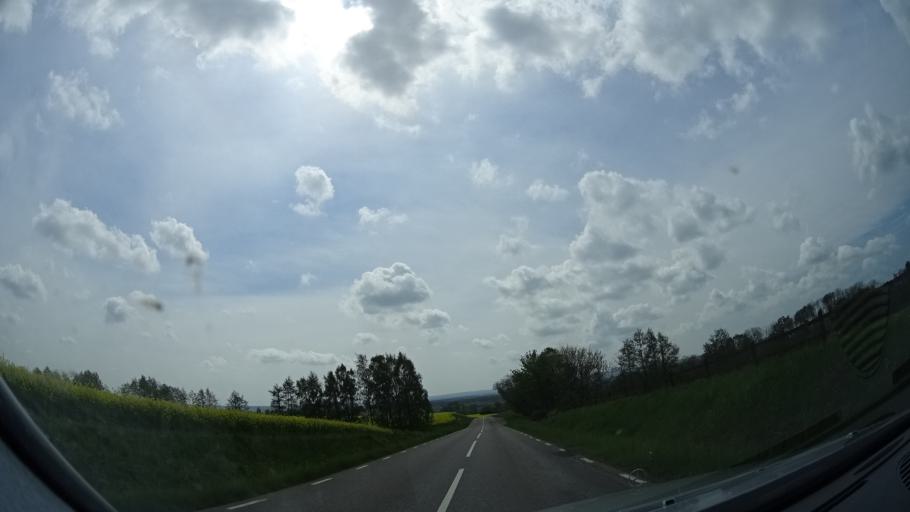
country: SE
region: Skane
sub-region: Hoors Kommun
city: Loberod
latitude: 55.7366
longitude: 13.4951
